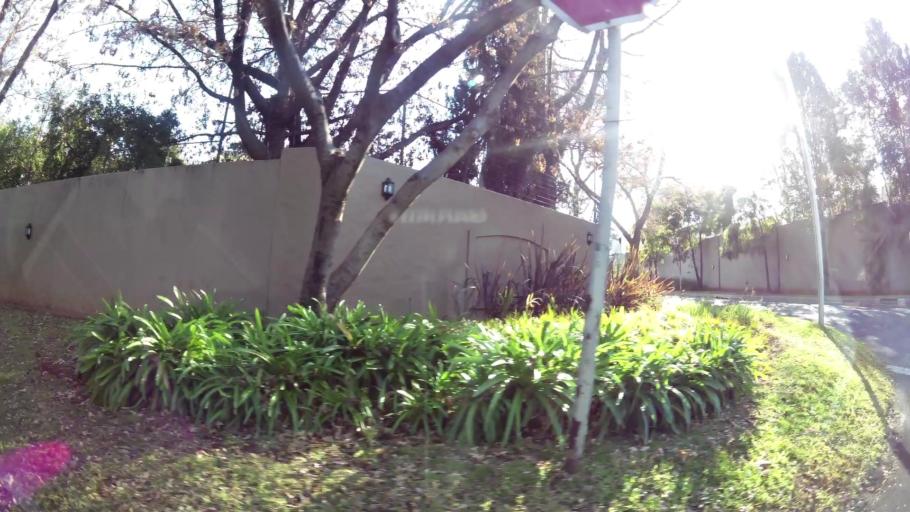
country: ZA
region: Gauteng
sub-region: City of Johannesburg Metropolitan Municipality
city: Johannesburg
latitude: -26.1112
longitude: 28.0706
